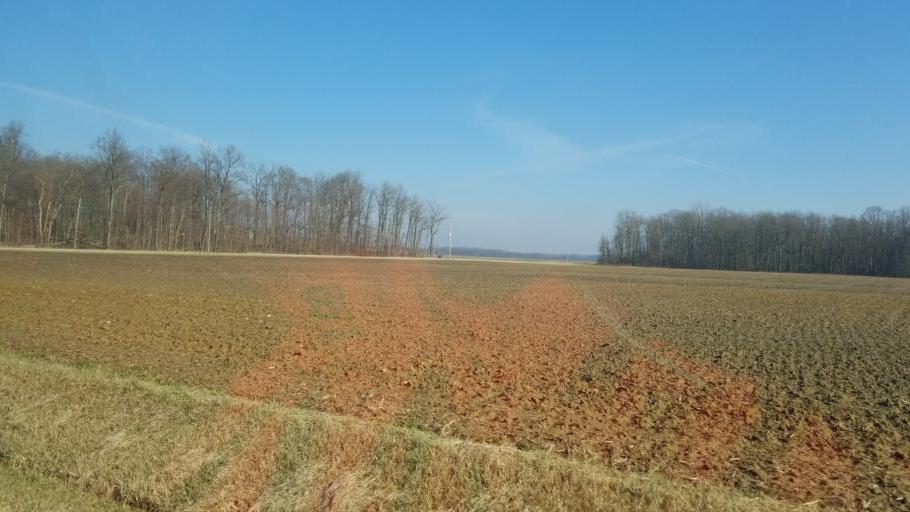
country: US
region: Ohio
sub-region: Crawford County
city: Bucyrus
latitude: 40.8910
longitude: -82.9881
